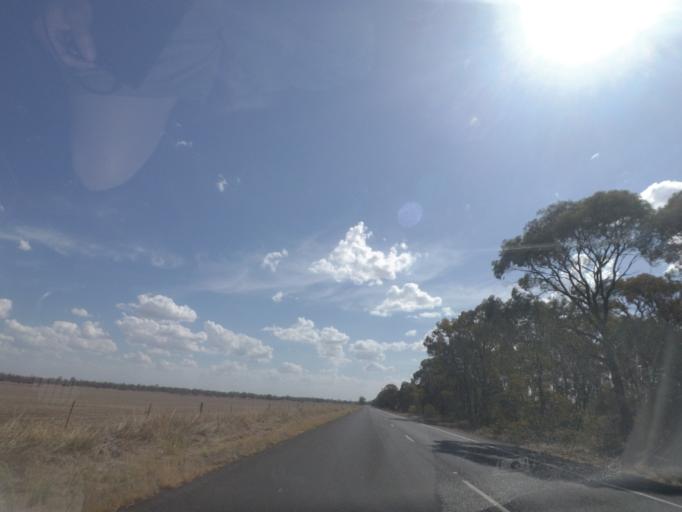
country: AU
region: Queensland
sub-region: Southern Downs
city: Stanthorpe
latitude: -28.4062
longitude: 151.1757
